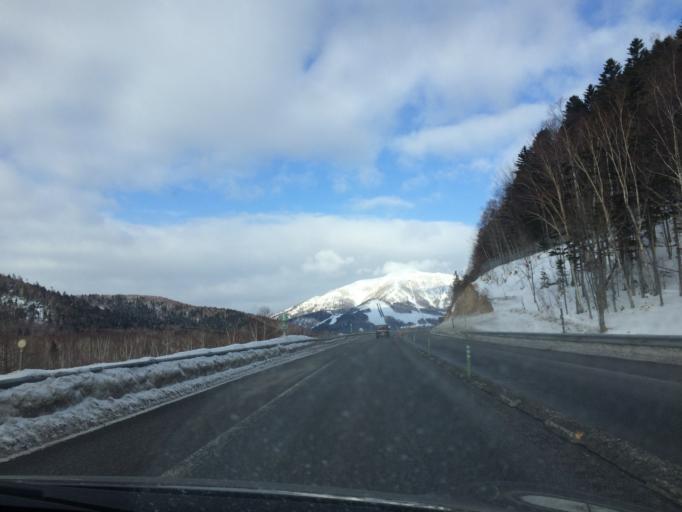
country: JP
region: Hokkaido
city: Shimo-furano
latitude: 43.0454
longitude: 142.6562
